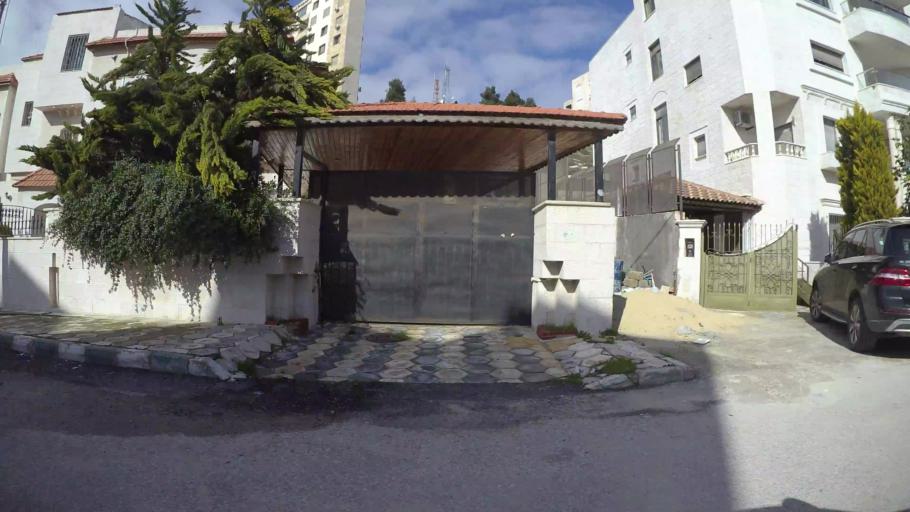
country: JO
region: Amman
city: Al Jubayhah
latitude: 32.0060
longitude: 35.8453
